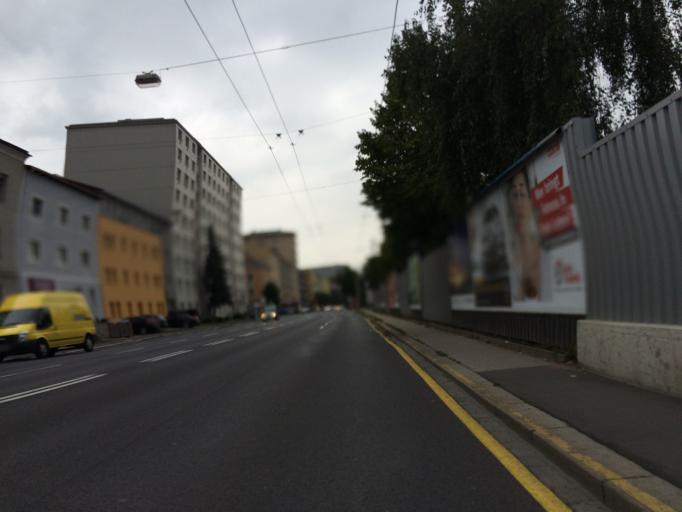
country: AT
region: Upper Austria
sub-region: Linz Stadt
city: Linz
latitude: 48.2885
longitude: 14.2965
